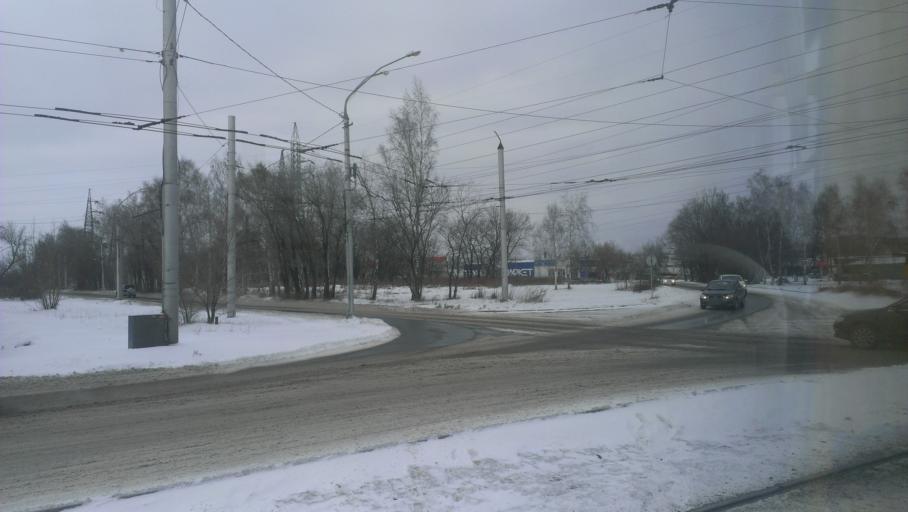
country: RU
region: Altai Krai
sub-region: Gorod Barnaulskiy
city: Barnaul
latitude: 53.3859
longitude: 83.7130
